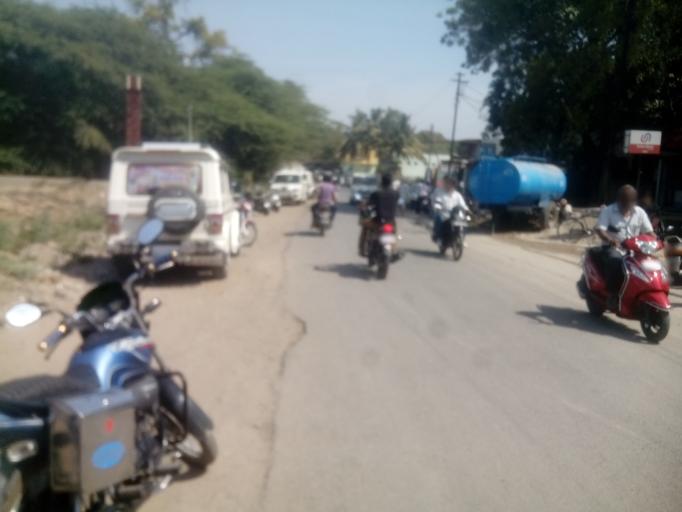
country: IN
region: Maharashtra
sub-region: Solapur
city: Sangola
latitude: 17.4362
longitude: 75.1891
